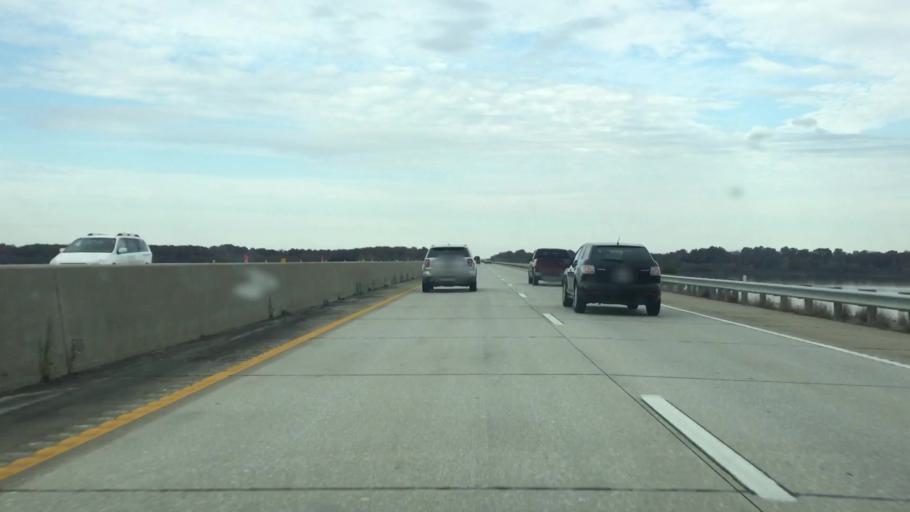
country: US
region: Missouri
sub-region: Henry County
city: Clinton
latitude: 38.2790
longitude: -93.7597
